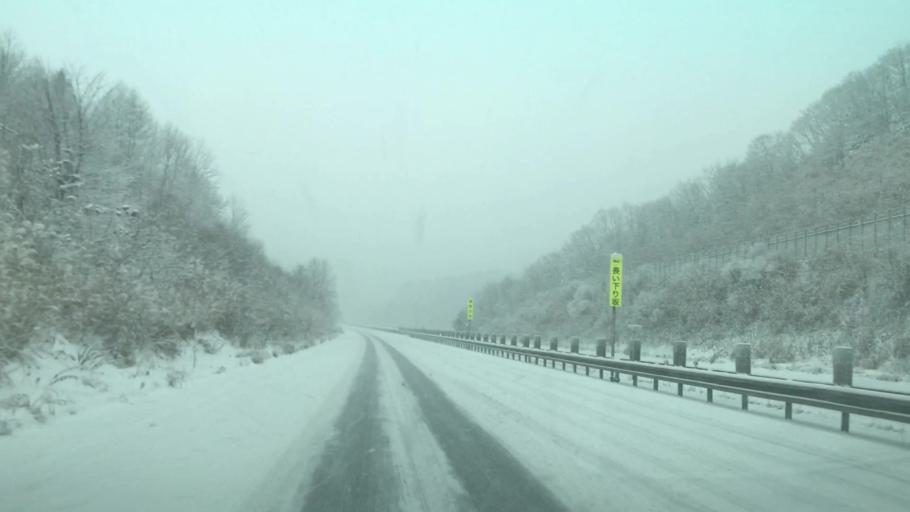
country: JP
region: Hokkaido
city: Muroran
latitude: 42.4288
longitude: 141.0995
